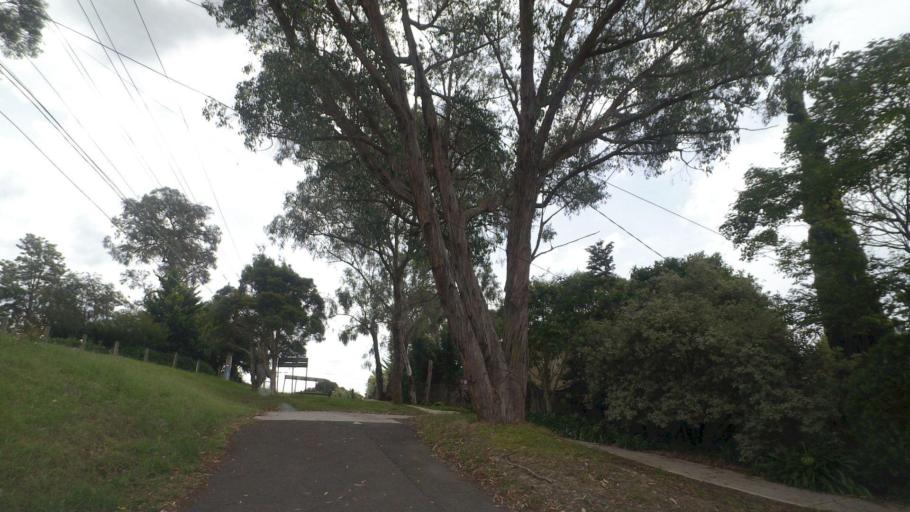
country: AU
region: Victoria
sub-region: Yarra Ranges
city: Lilydale
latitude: -37.7608
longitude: 145.3584
